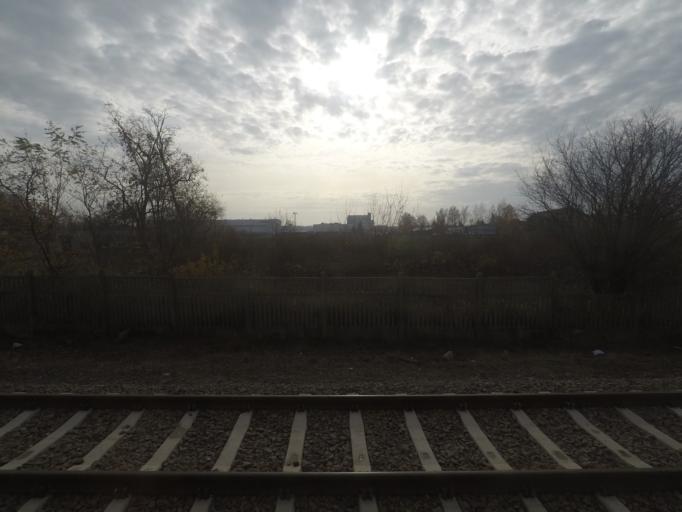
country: PL
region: Subcarpathian Voivodeship
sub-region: Powiat ropczycko-sedziszowski
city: Ostrow
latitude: 50.0792
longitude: 21.5880
